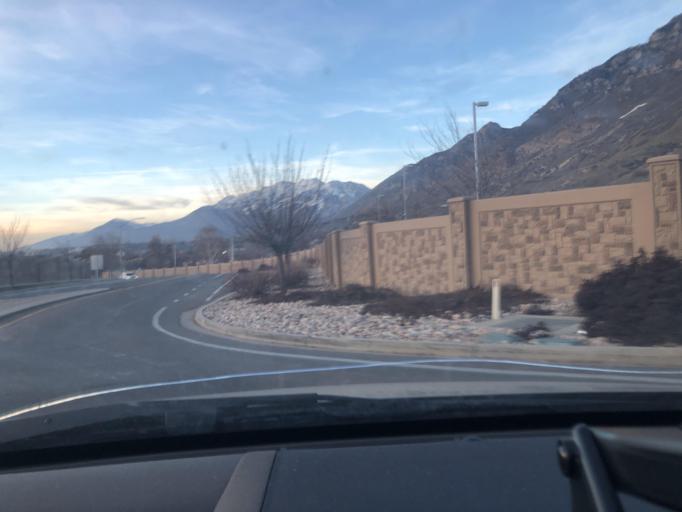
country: US
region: Utah
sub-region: Utah County
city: Provo
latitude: 40.2298
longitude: -111.6351
